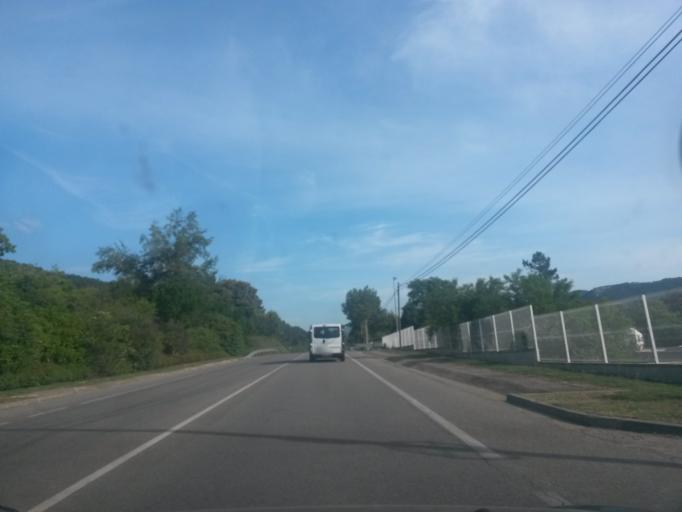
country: ES
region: Catalonia
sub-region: Provincia de Girona
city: la Cellera de Ter
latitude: 41.9963
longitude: 2.6084
